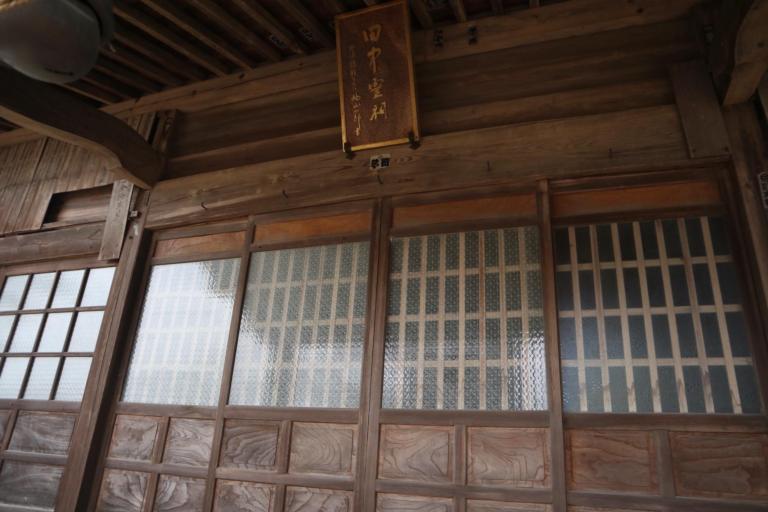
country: JP
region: Tochigi
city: Fujioka
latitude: 36.2684
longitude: 139.6419
